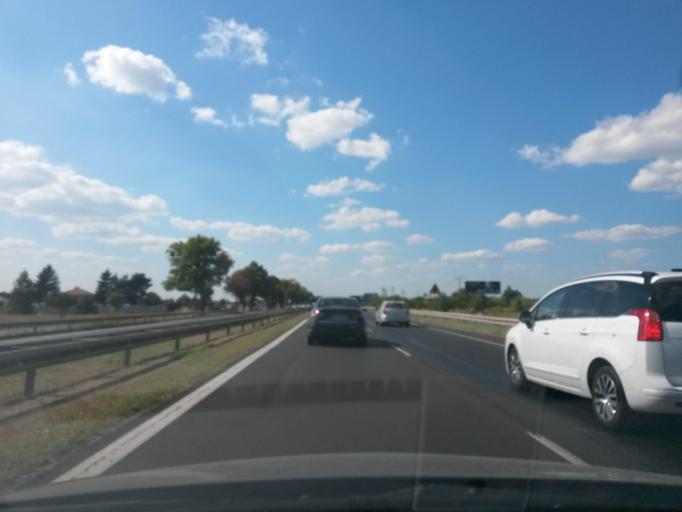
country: PL
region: Masovian Voivodeship
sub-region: Powiat warszawski zachodni
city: Dziekanow Lesny
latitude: 52.3648
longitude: 20.8127
